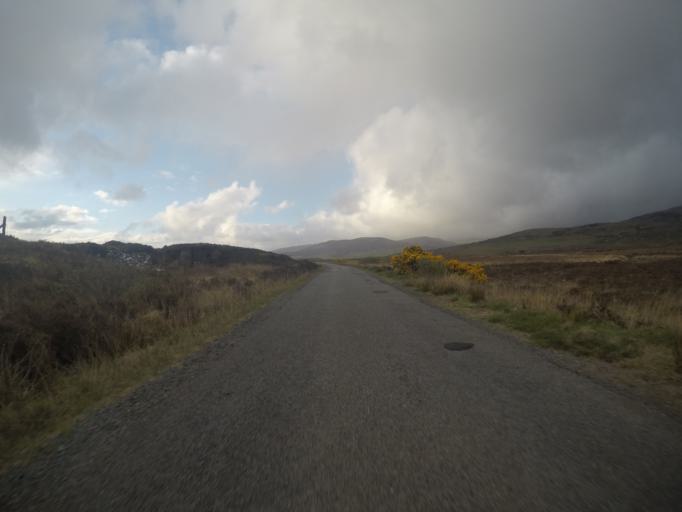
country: GB
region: Scotland
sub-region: Highland
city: Isle of Skye
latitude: 57.4603
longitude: -6.2967
